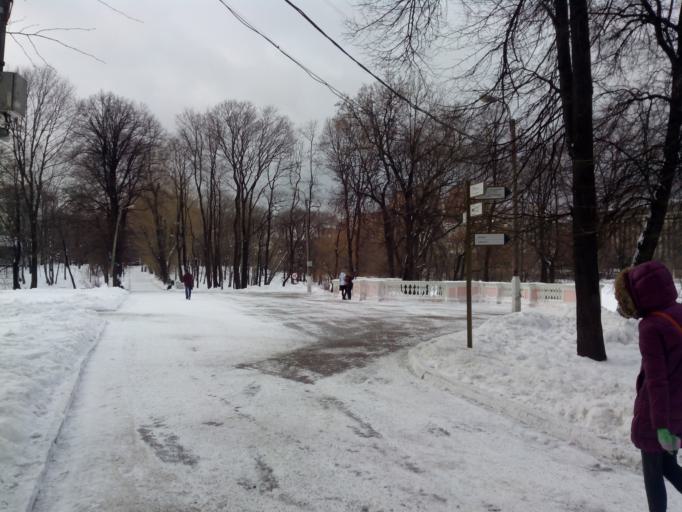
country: RU
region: Moscow
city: Lefortovo
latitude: 55.7640
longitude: 37.6905
